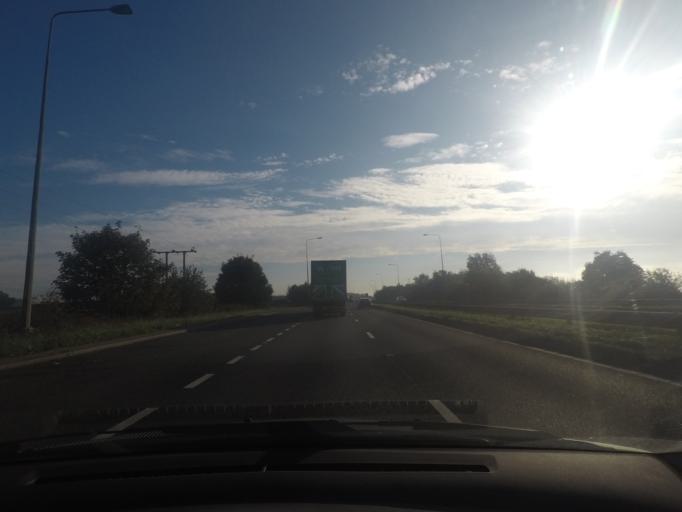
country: GB
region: England
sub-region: East Riding of Yorkshire
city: North Ferriby
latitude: 53.7255
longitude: -0.4886
